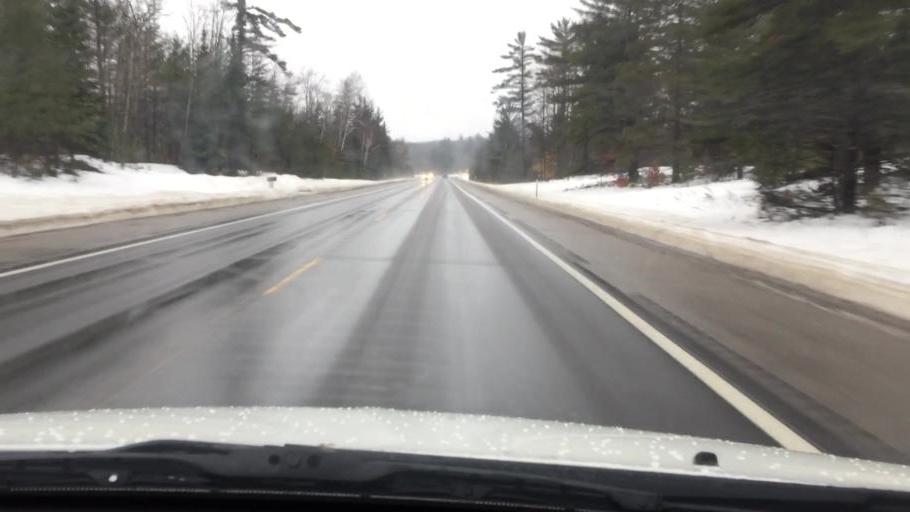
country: US
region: Michigan
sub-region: Kalkaska County
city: Kalkaska
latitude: 44.6473
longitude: -85.2747
